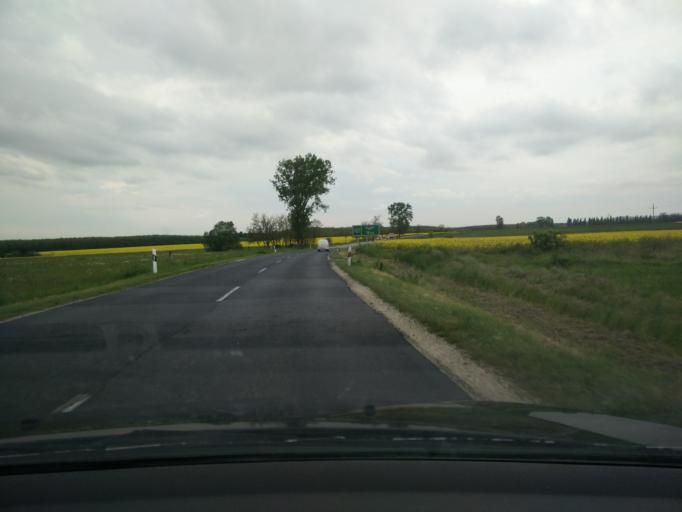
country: HU
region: Gyor-Moson-Sopron
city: Tet
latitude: 47.5258
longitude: 17.5197
